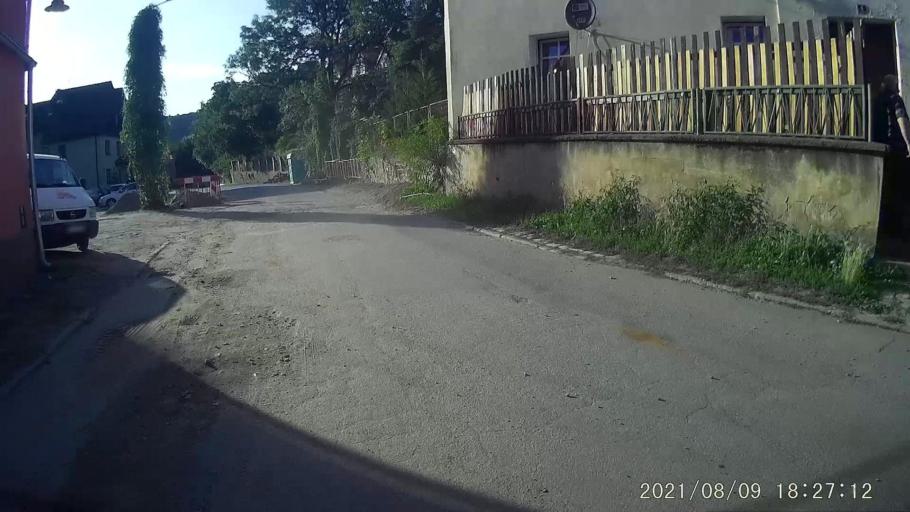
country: PL
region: Lower Silesian Voivodeship
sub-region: Powiat zabkowicki
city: Bardo
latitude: 50.5067
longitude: 16.7395
